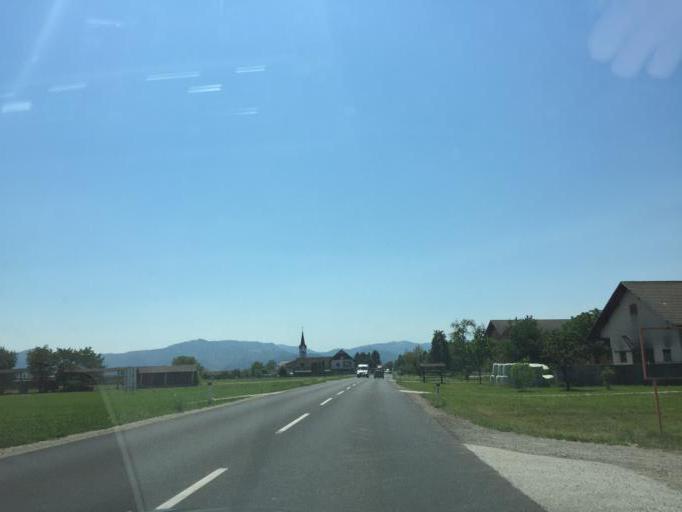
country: SI
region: Kranj
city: Zgornje Bitnje
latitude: 46.2112
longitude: 14.3367
